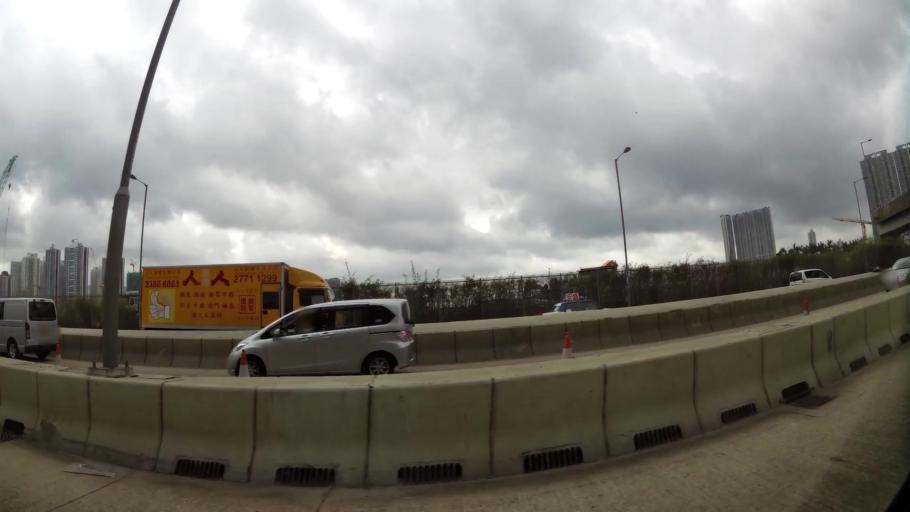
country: HK
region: Kowloon City
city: Kowloon
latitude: 22.3295
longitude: 114.1933
